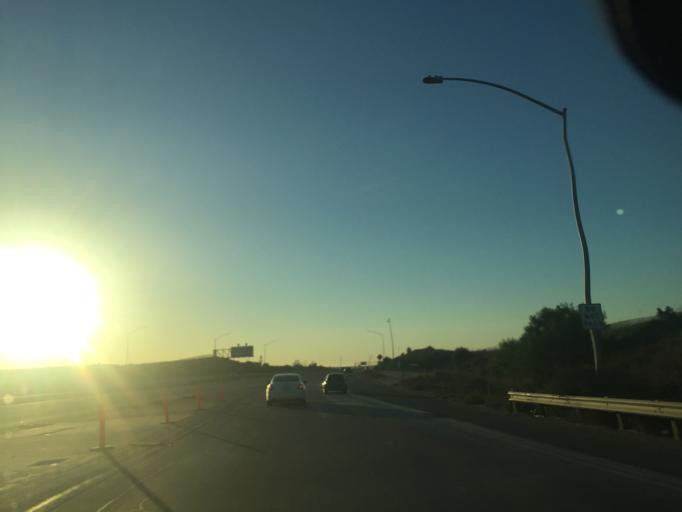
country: MX
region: Baja California
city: Tijuana
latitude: 32.5643
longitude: -116.9289
